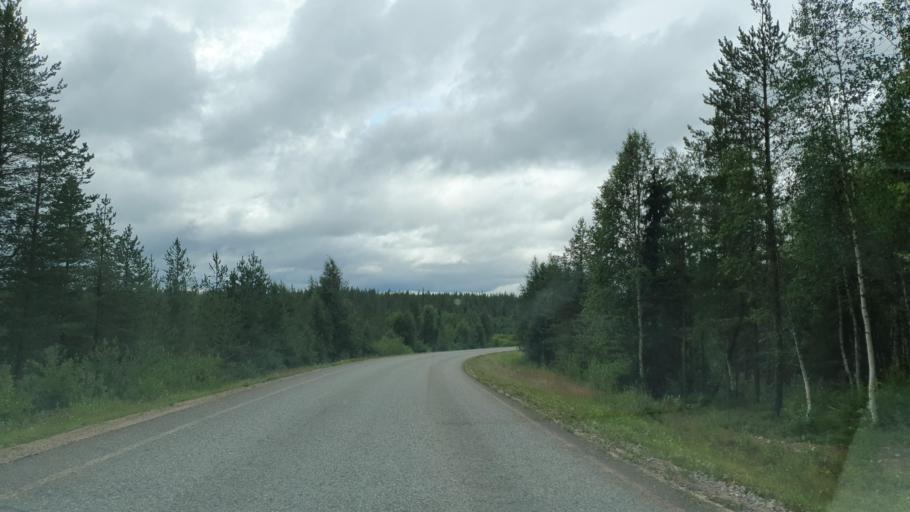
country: FI
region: Lapland
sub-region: Tunturi-Lappi
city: Kolari
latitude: 67.5071
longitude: 24.2363
